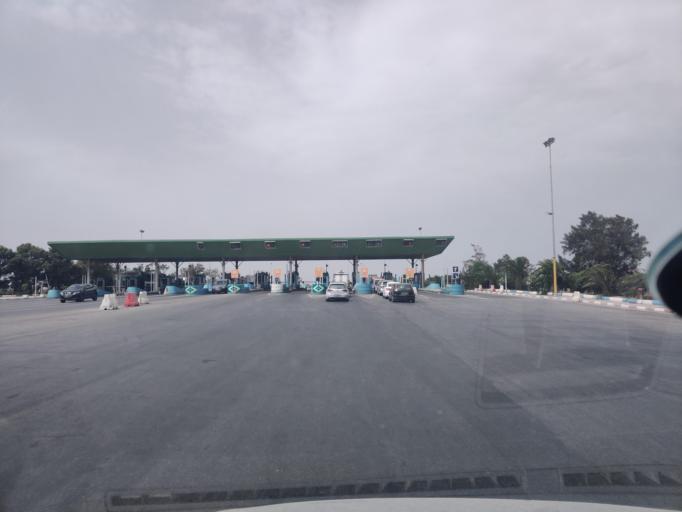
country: TN
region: Susah
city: Sidi Bou Ali
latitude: 36.0031
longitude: 10.4360
